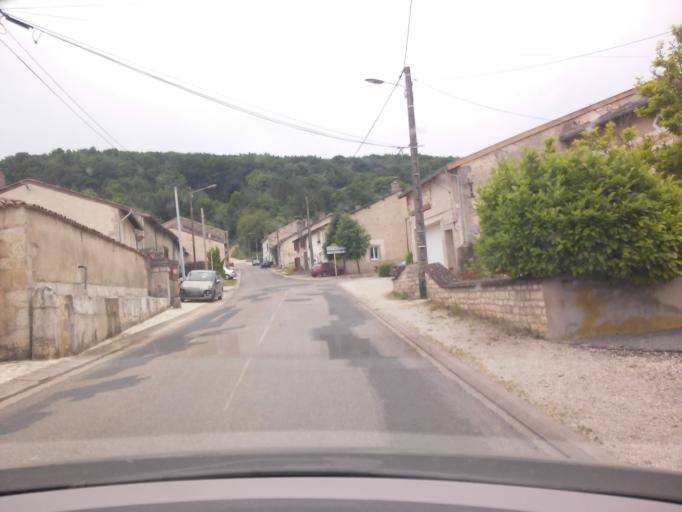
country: FR
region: Lorraine
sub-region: Departement de la Meuse
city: Vignot
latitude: 48.8005
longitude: 5.6541
